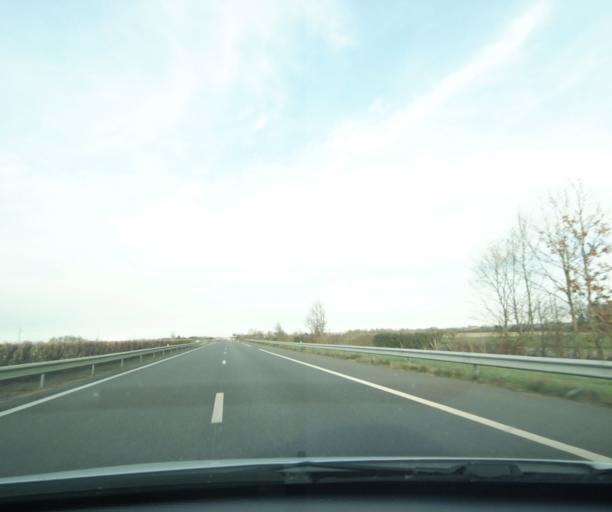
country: FR
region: Midi-Pyrenees
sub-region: Departement de la Haute-Garonne
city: Cazeres
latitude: 43.2329
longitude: 1.0687
